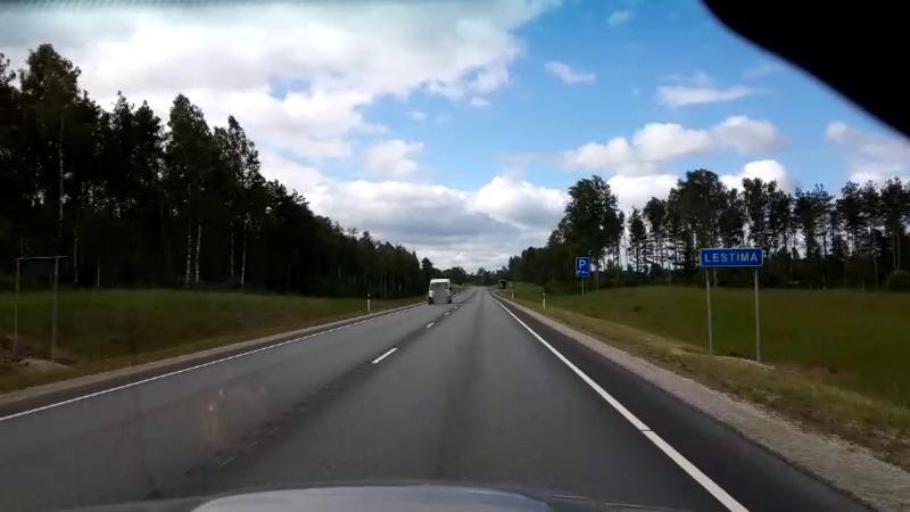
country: EE
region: Harju
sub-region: Nissi vald
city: Riisipere
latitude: 59.0809
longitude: 24.4568
